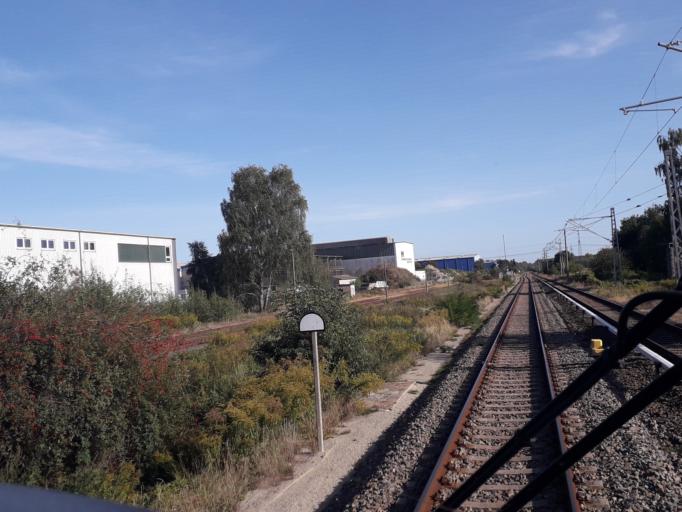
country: DE
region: Brandenburg
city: Velten
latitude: 52.6798
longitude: 13.1798
